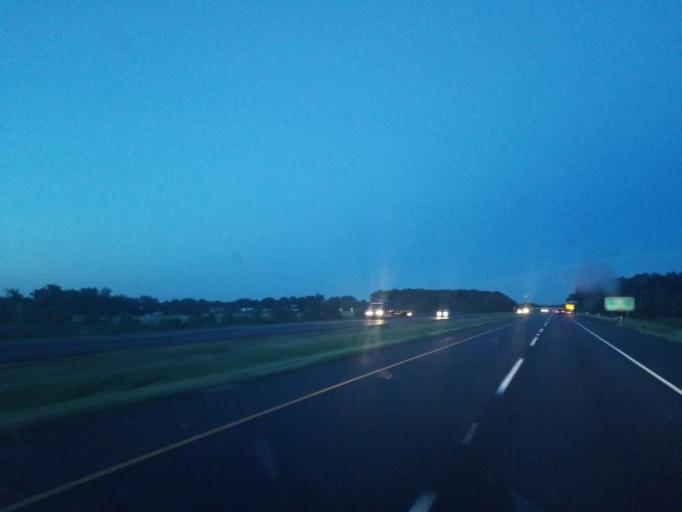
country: US
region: Indiana
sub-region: Saint Joseph County
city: Granger
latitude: 41.7311
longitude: -86.0781
